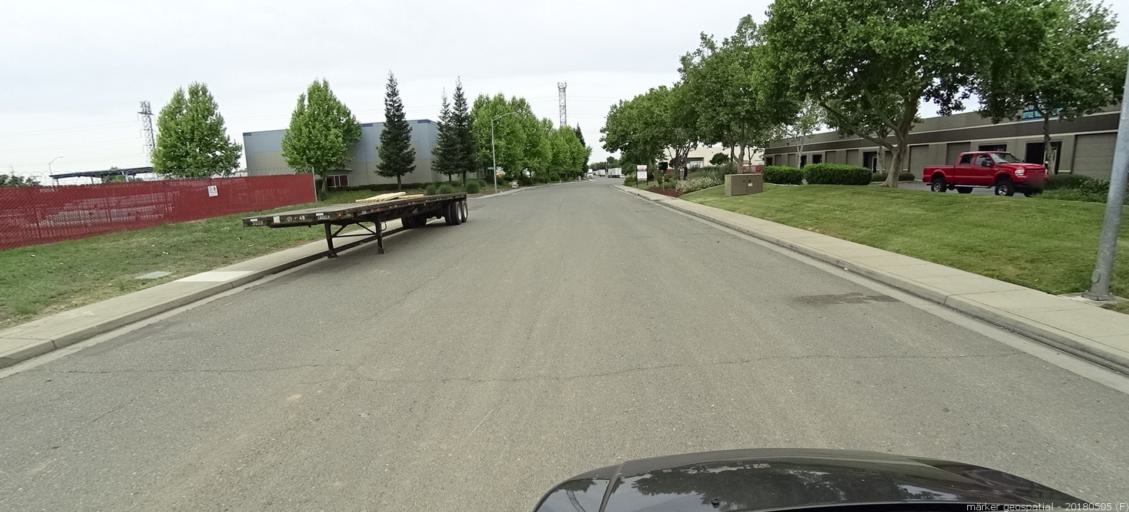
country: US
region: California
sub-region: Sacramento County
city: Rio Linda
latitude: 38.6490
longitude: -121.4216
